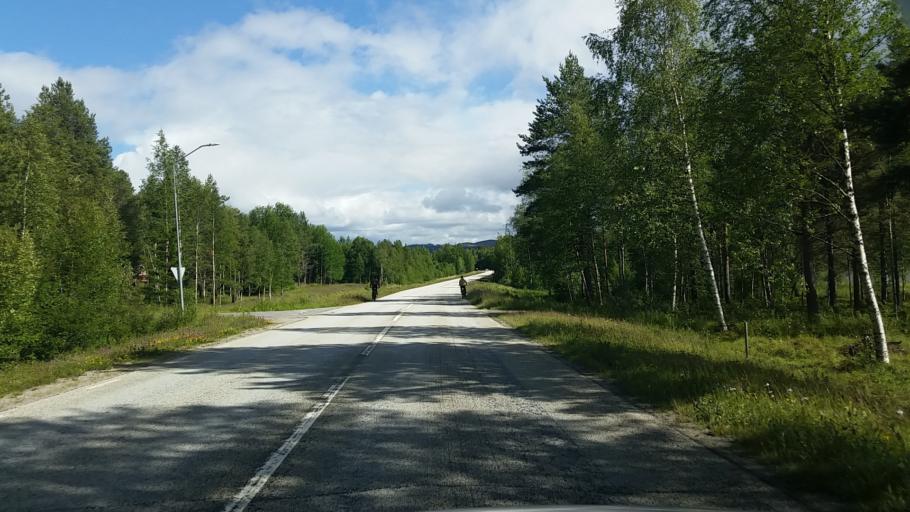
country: SE
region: Jaemtland
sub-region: Harjedalens Kommun
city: Sveg
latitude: 62.4113
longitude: 13.6803
